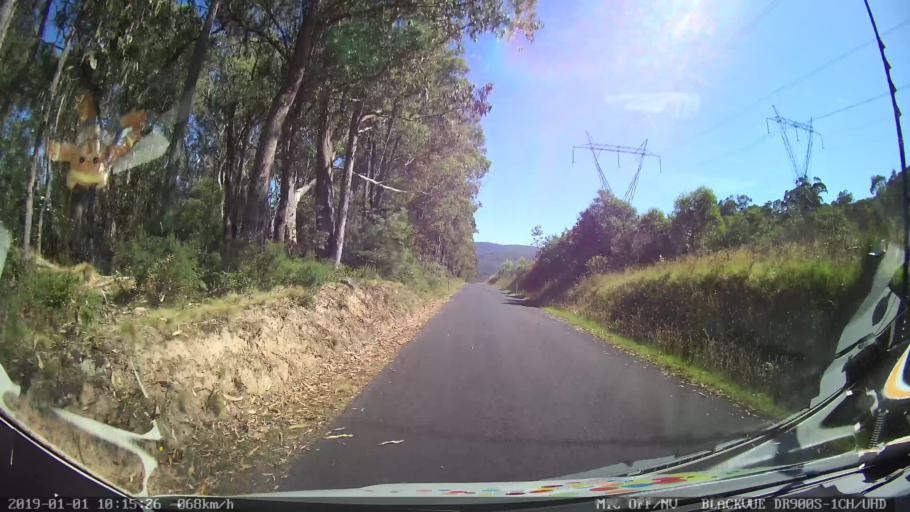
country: AU
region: New South Wales
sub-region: Snowy River
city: Jindabyne
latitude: -36.1016
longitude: 148.1620
